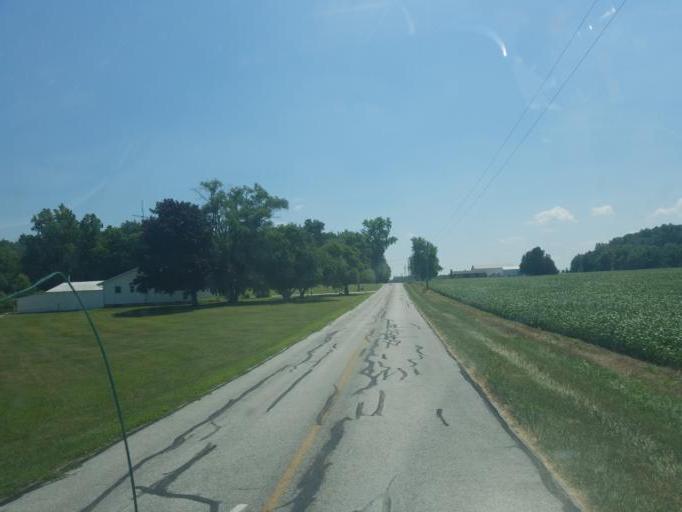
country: US
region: Ohio
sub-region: Shelby County
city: Botkins
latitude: 40.4935
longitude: -84.2310
